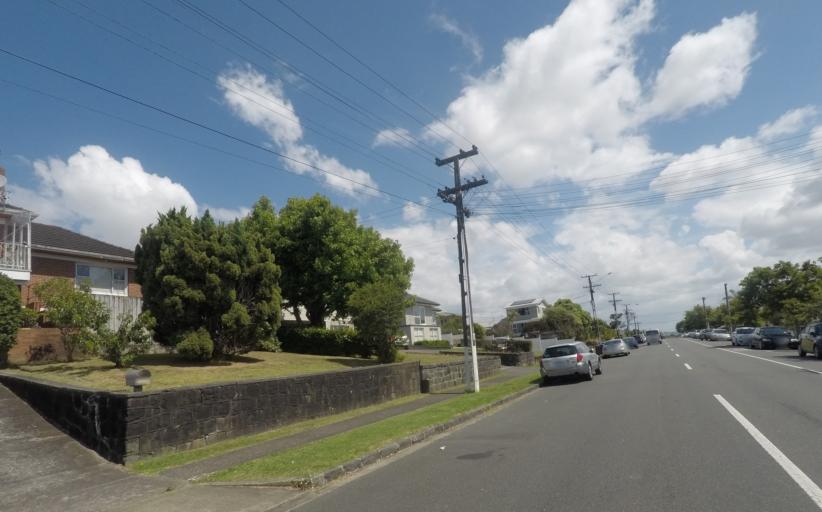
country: NZ
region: Auckland
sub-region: Auckland
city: Tamaki
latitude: -36.8947
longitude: 174.8107
